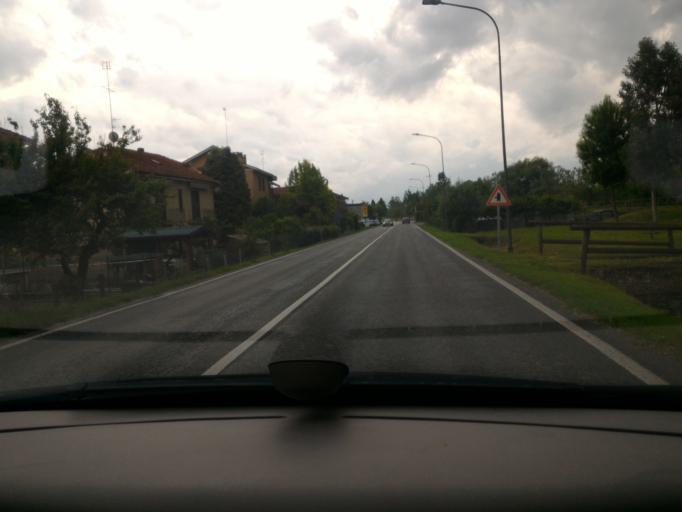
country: IT
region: Piedmont
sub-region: Provincia di Cuneo
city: Savigliano
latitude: 44.6462
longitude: 7.6502
